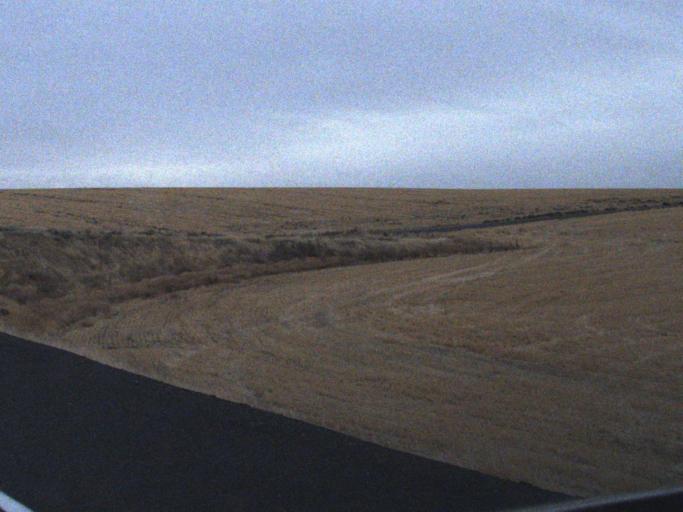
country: US
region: Washington
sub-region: Franklin County
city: Connell
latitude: 46.7939
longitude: -118.7315
